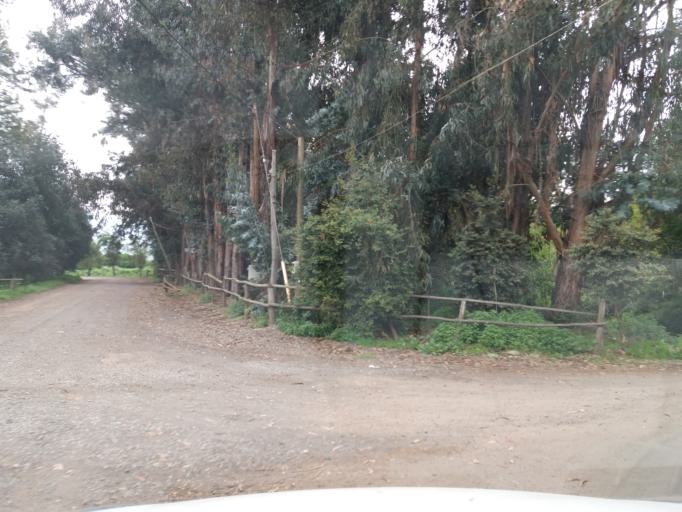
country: CL
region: Valparaiso
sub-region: Provincia de Quillota
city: Hacienda La Calera
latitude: -32.8567
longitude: -71.1040
